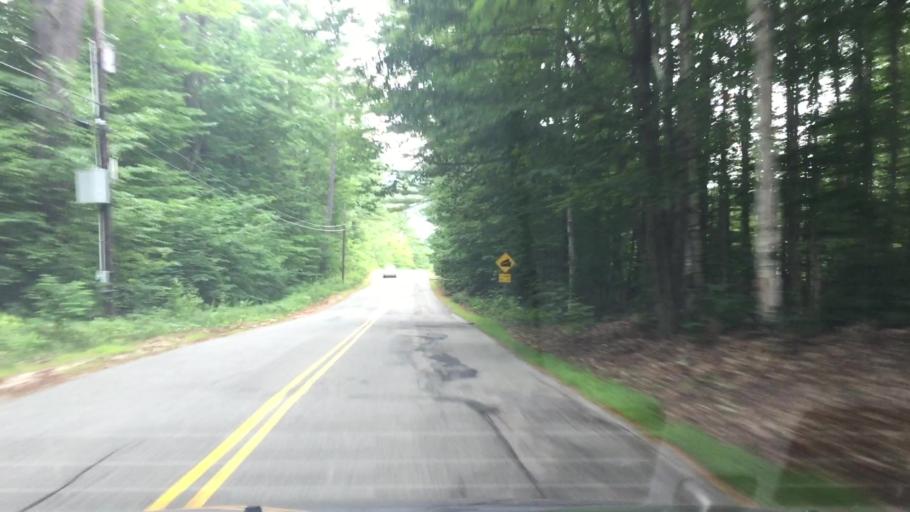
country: US
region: New Hampshire
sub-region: Carroll County
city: North Conway
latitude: 44.0764
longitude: -71.1343
